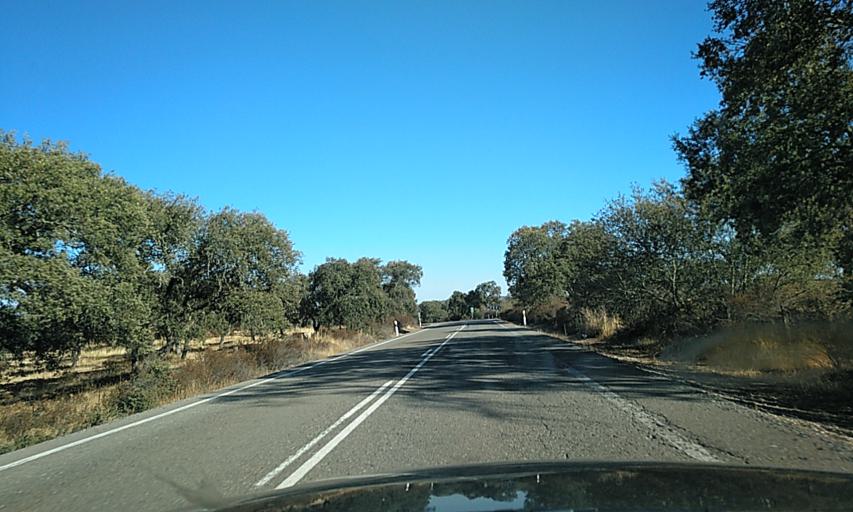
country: ES
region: Andalusia
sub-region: Provincia de Huelva
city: Santa Barbara de Casa
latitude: 37.7688
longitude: -7.1413
